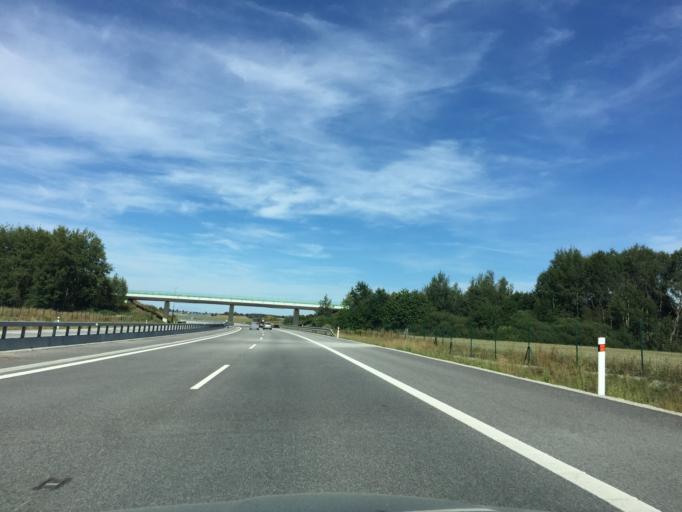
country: CZ
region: Jihocesky
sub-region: Okres Tabor
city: Veseli nad Luznici
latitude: 49.1723
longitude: 14.6757
